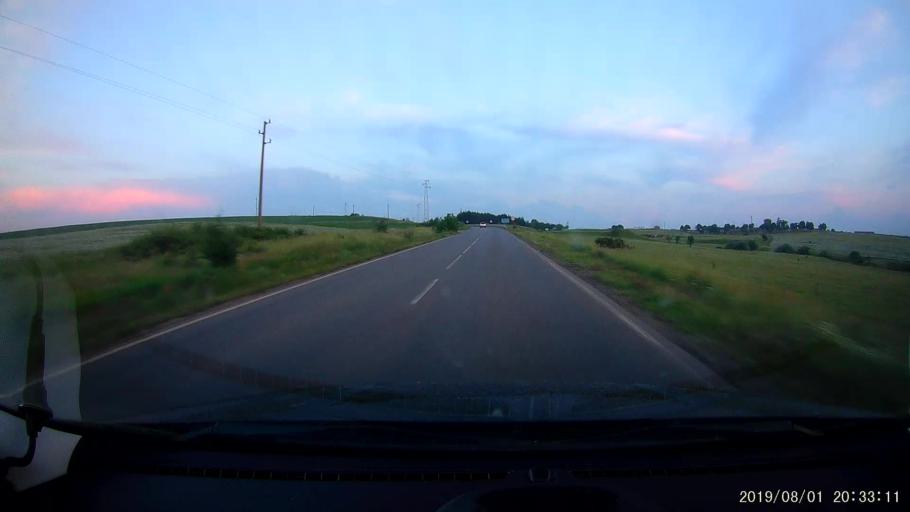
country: BG
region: Yambol
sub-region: Obshtina Elkhovo
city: Elkhovo
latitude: 42.1096
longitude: 26.5323
